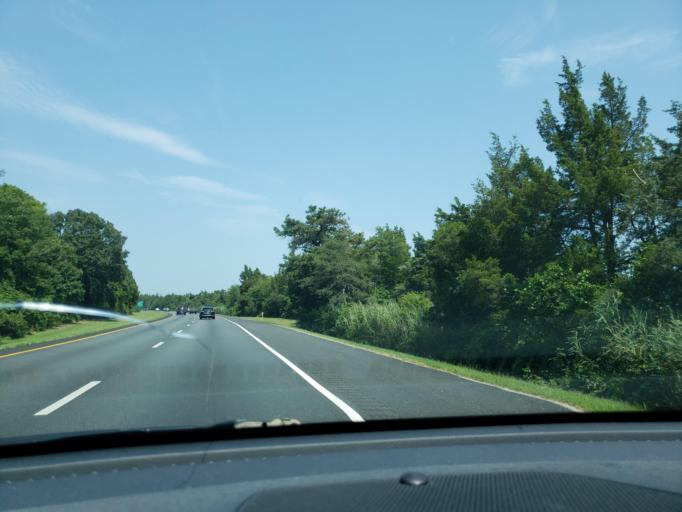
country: US
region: New Jersey
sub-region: Cape May County
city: Ocean City
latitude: 39.2752
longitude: -74.6289
